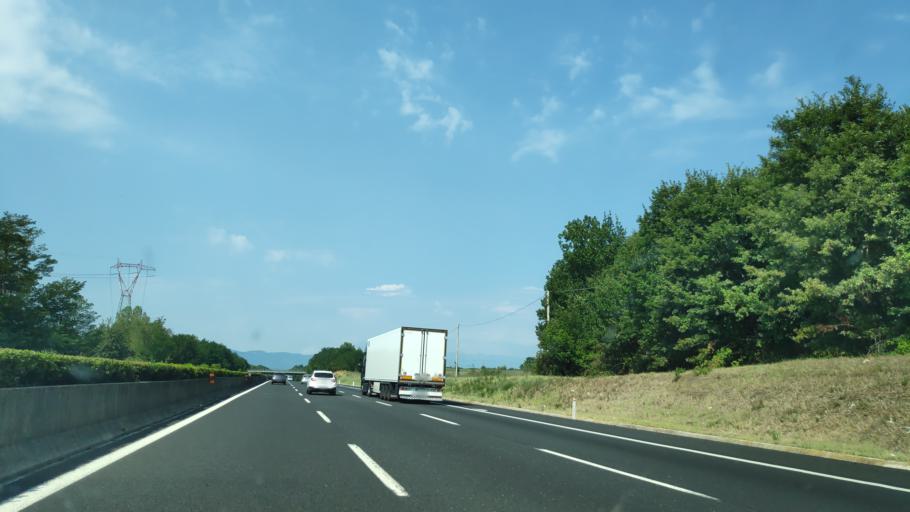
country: IT
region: Latium
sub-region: Provincia di Frosinone
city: Ceprano
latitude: 41.5442
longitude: 13.5549
